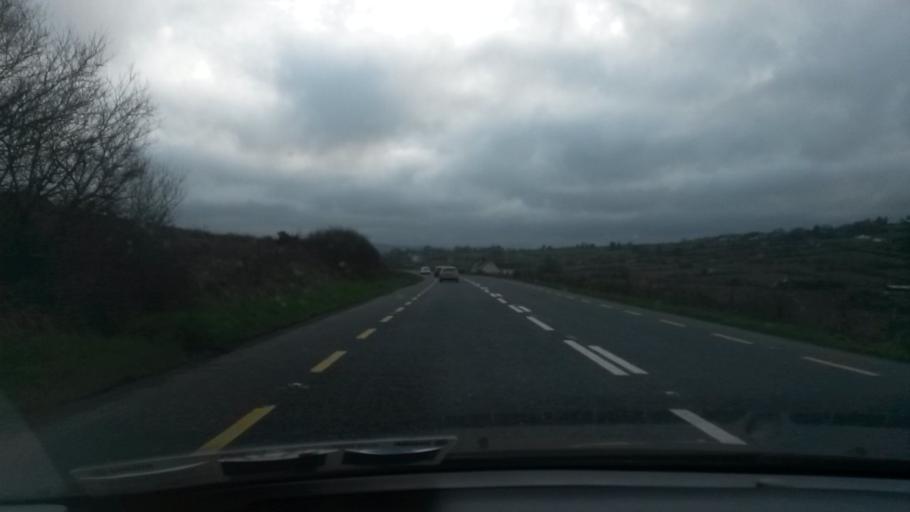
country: IE
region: Munster
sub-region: County Limerick
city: Newcastle West
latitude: 52.4079
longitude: -9.1631
